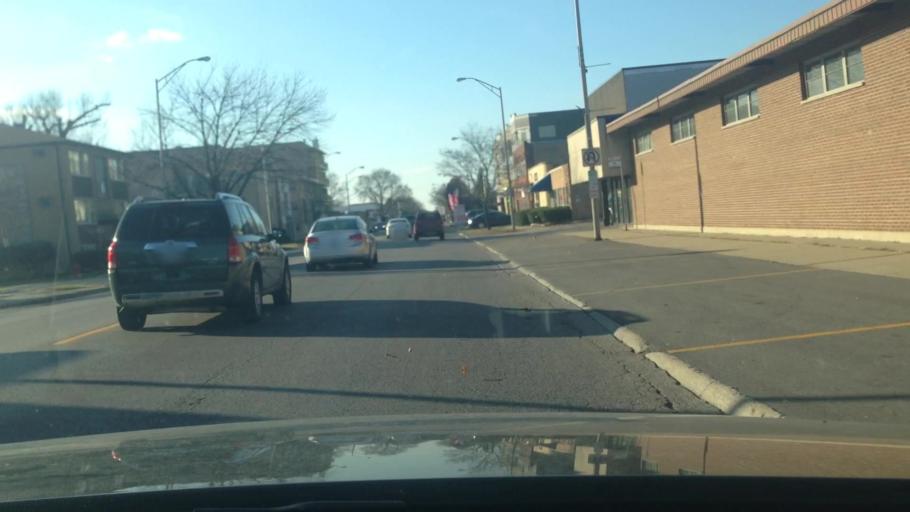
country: US
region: Illinois
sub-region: Cook County
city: River Grove
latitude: 41.9267
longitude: -87.8228
